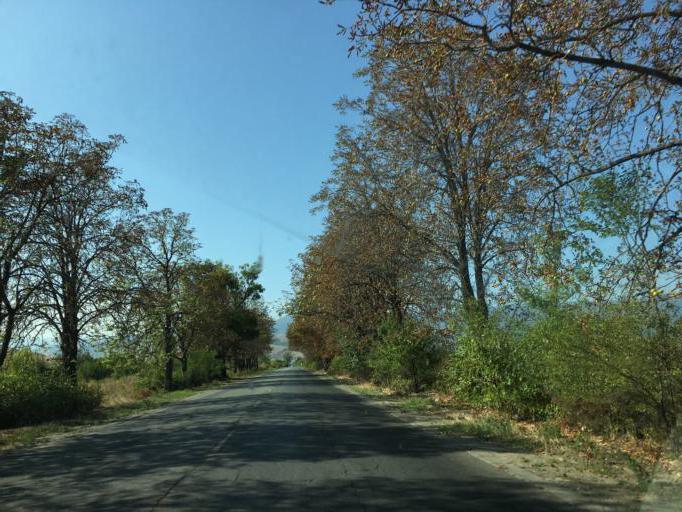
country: BG
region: Pazardzhik
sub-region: Obshtina Pazardzhik
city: Pazardzhik
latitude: 42.1483
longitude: 24.3061
